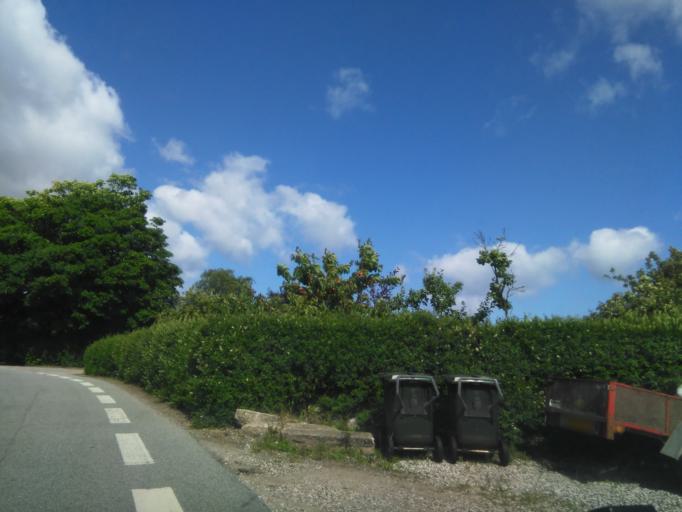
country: DK
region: Central Jutland
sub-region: Syddjurs Kommune
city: Ronde
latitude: 56.1802
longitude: 10.5106
